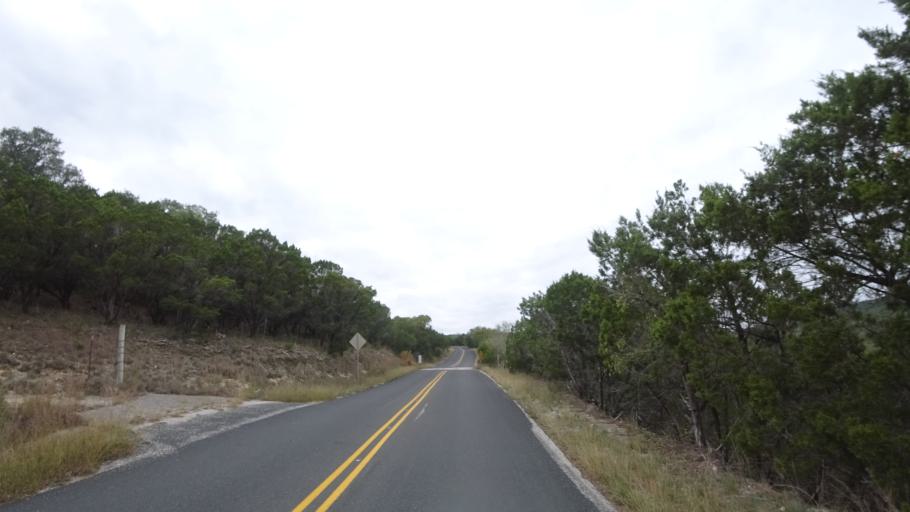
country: US
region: Texas
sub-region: Travis County
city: Bee Cave
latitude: 30.3543
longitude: -97.9230
